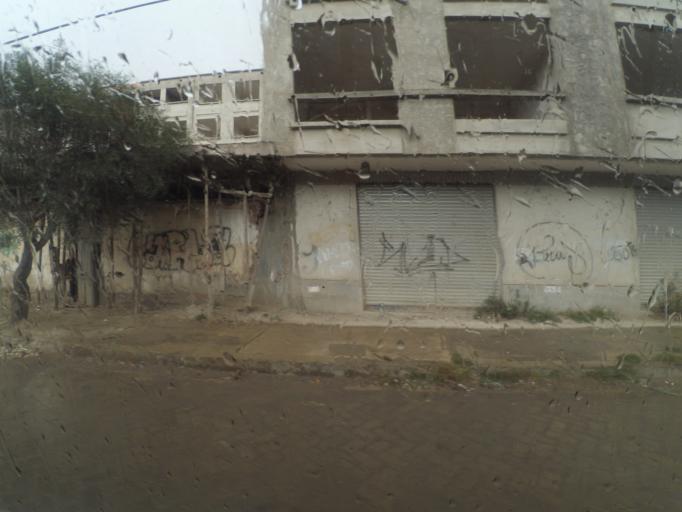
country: BO
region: La Paz
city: La Paz
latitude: -16.5194
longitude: -68.1665
